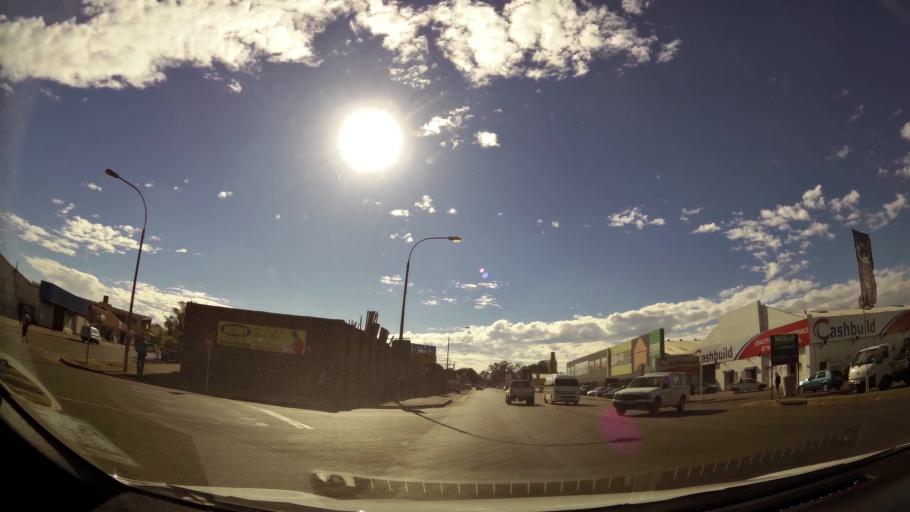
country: ZA
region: Limpopo
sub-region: Waterberg District Municipality
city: Bela-Bela
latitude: -24.8860
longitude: 28.2971
